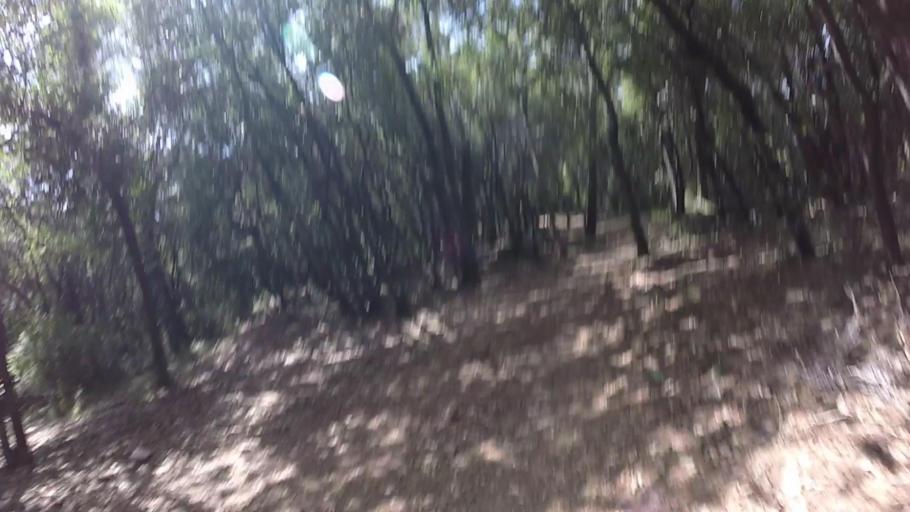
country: FR
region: Provence-Alpes-Cote d'Azur
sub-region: Departement des Alpes-Maritimes
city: Mougins
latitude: 43.6151
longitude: 7.0278
